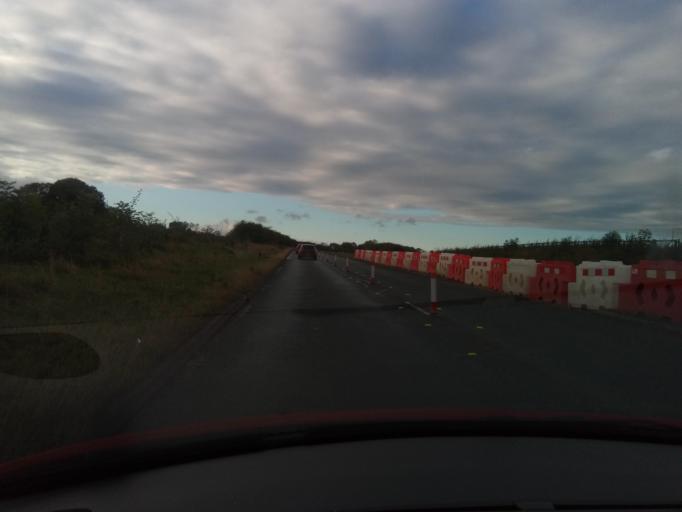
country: GB
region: England
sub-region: Darlington
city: Heighington
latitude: 54.5666
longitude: -1.6029
